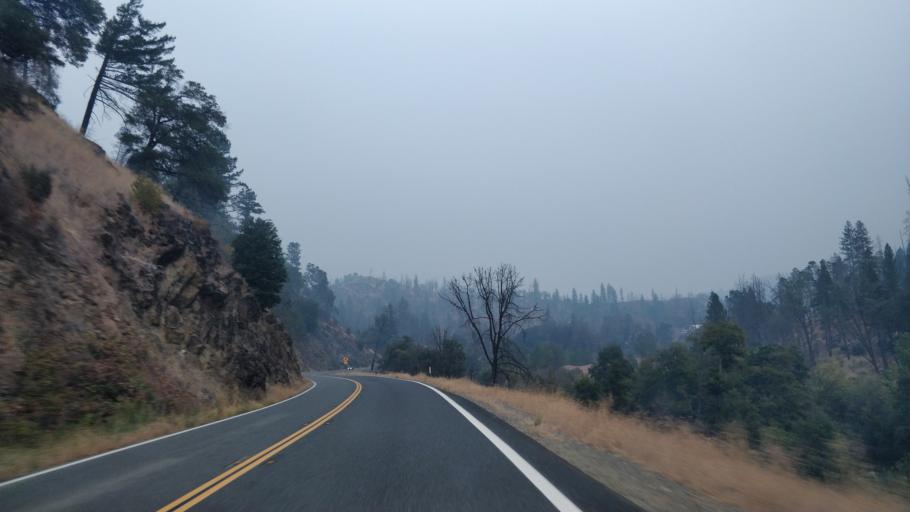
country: US
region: California
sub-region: Trinity County
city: Weaverville
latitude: 40.7665
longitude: -123.1090
